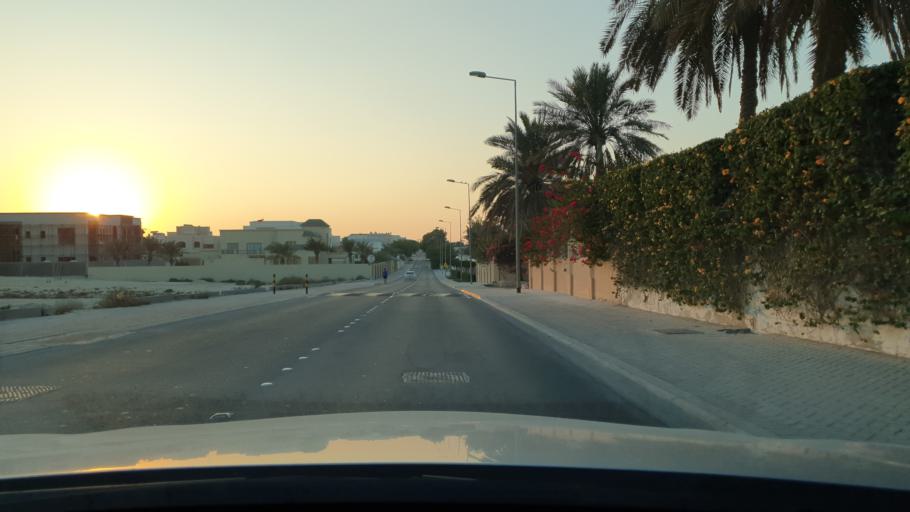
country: BH
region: Northern
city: Ar Rifa'
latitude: 26.1412
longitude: 50.5310
